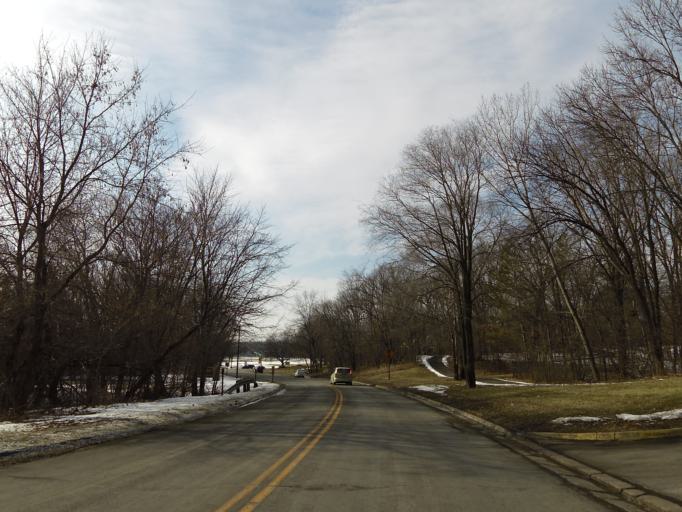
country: US
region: Minnesota
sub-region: Hennepin County
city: Eden Prairie
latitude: 44.8443
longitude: -93.4214
